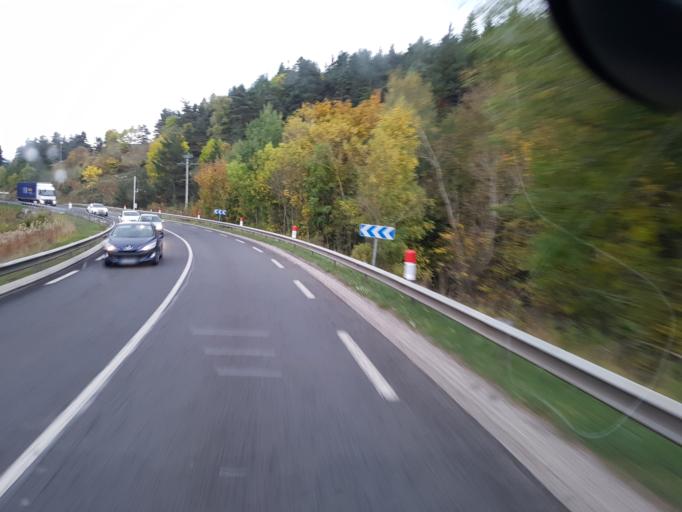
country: FR
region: Languedoc-Roussillon
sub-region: Departement de la Lozere
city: Mende
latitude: 44.5660
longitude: 3.6194
